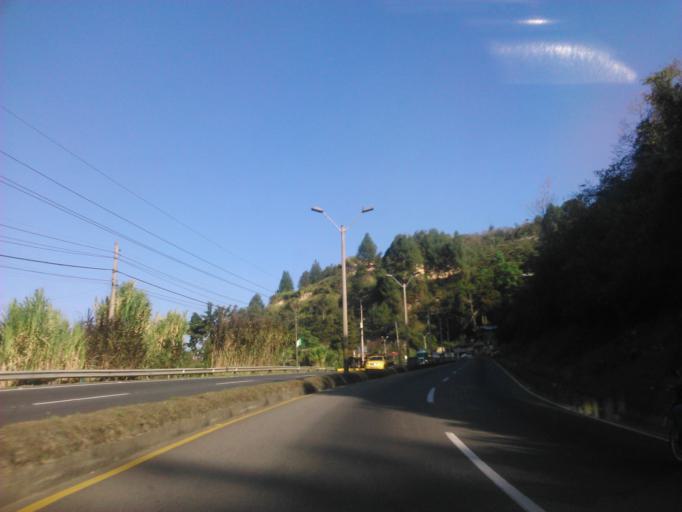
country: CO
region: Antioquia
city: Municipio de Copacabana
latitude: 6.3265
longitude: -75.4747
